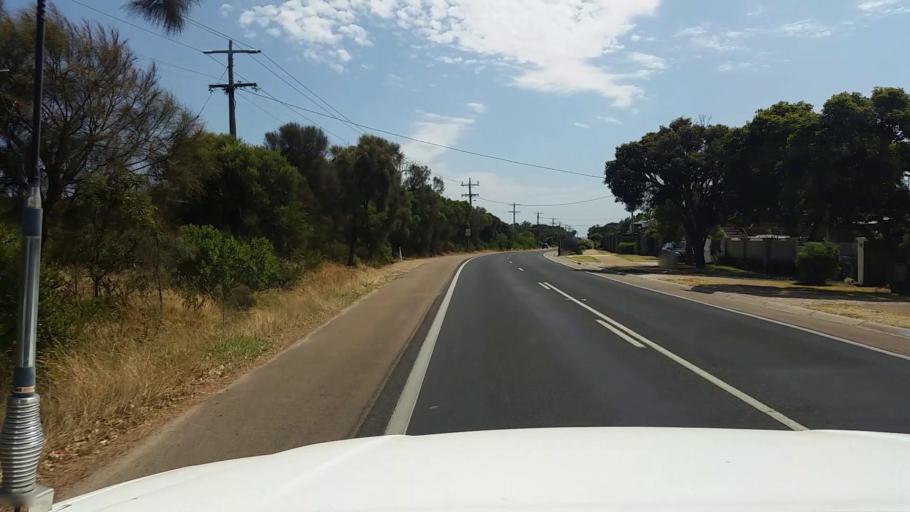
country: AU
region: Victoria
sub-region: Mornington Peninsula
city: Mornington
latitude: -38.2374
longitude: 145.0290
